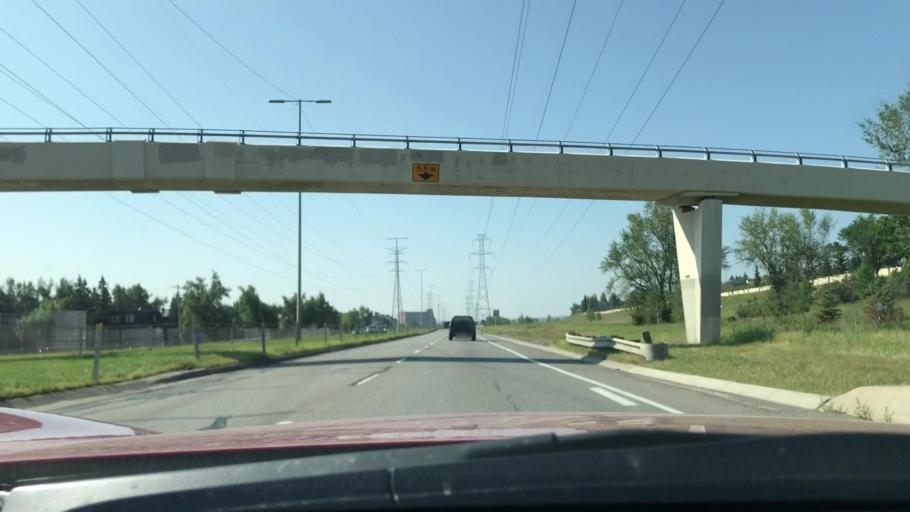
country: CA
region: Alberta
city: Calgary
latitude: 51.0318
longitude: -114.1645
